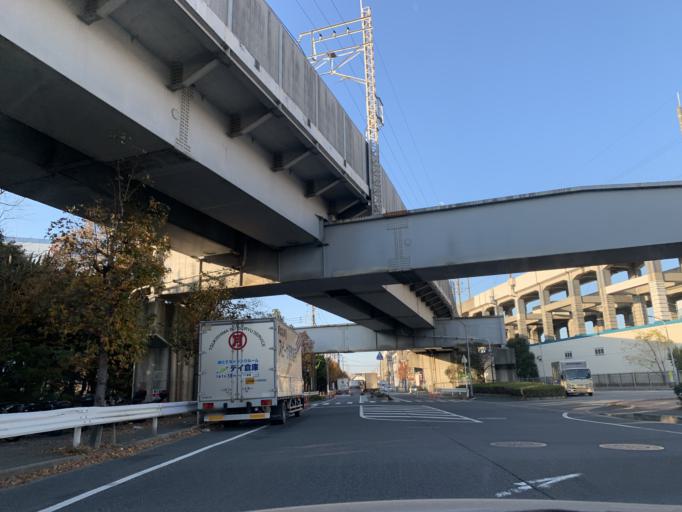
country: JP
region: Chiba
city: Funabashi
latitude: 35.6935
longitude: 139.9563
